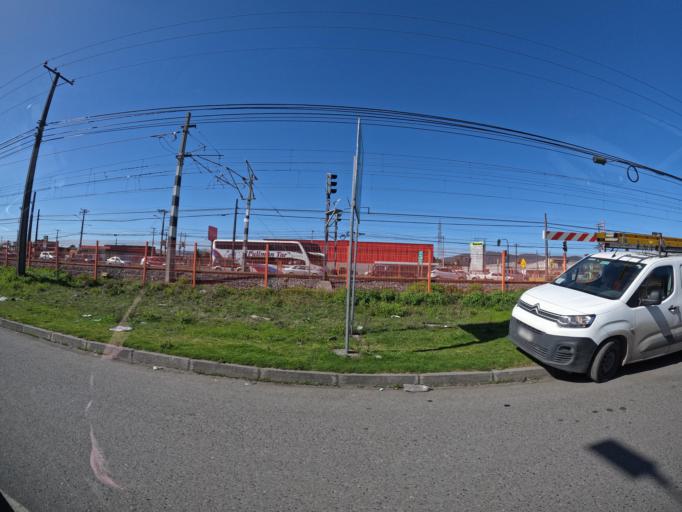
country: CL
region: Biobio
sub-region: Provincia de Concepcion
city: Concepcion
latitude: -36.8890
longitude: -73.1413
